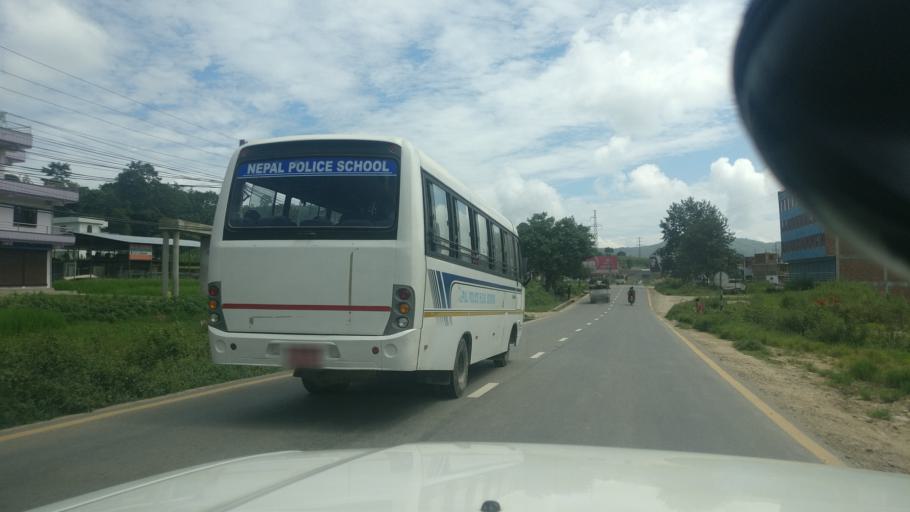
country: NP
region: Central Region
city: Banepa
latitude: 27.6322
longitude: 85.5010
